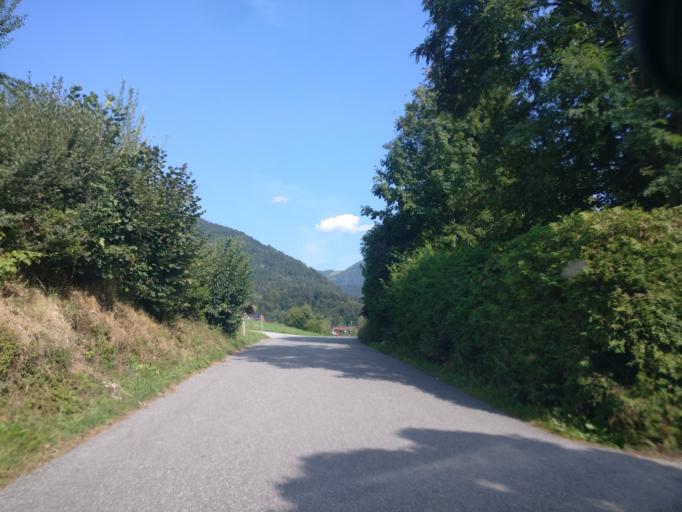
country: AT
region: Salzburg
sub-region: Politischer Bezirk Sankt Johann im Pongau
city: Pfarrwerfen
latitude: 47.4643
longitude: 13.2232
